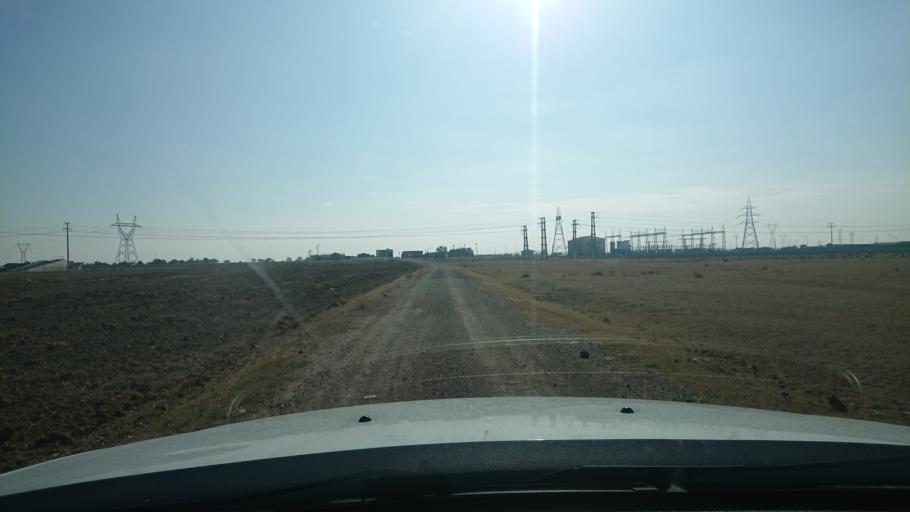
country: TR
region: Aksaray
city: Sultanhani
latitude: 38.2560
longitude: 33.4716
